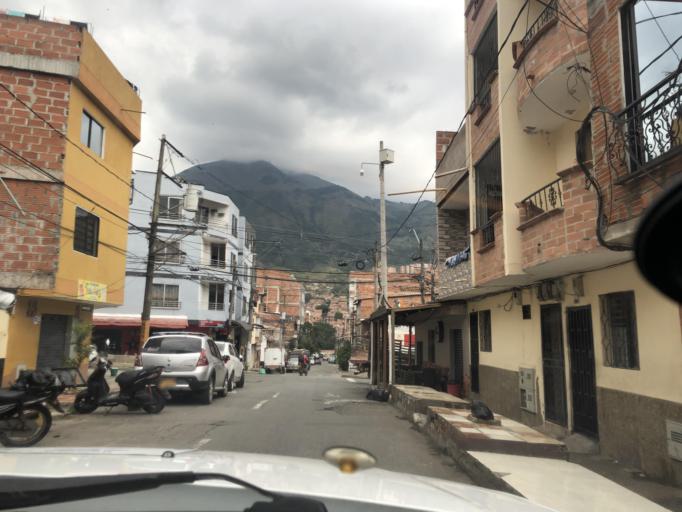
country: CO
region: Antioquia
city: Bello
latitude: 6.3399
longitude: -75.5613
